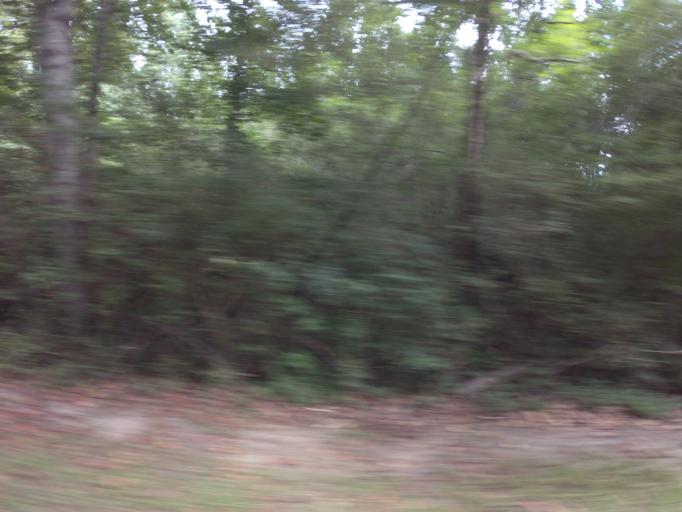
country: US
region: Georgia
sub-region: Gwinnett County
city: Duluth
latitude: 34.0406
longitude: -84.1350
